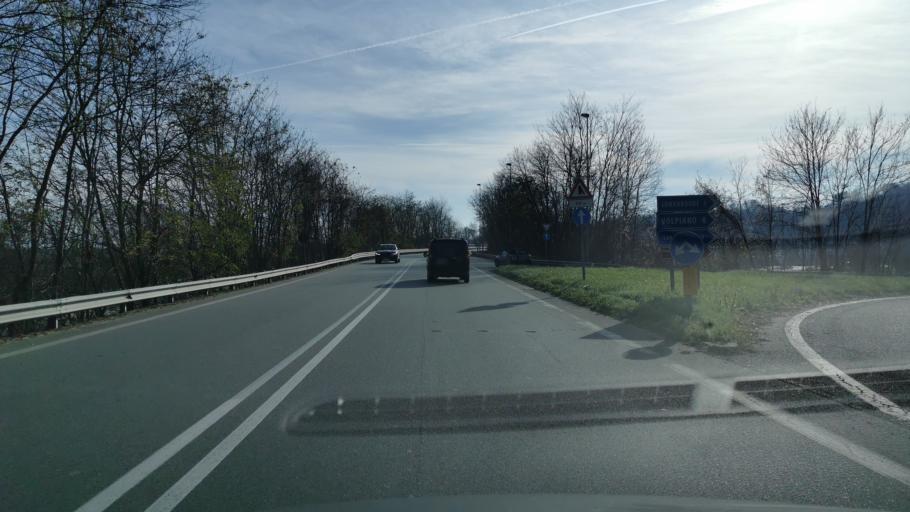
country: IT
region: Piedmont
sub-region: Provincia di Torino
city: Lombardore
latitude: 45.2340
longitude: 7.7477
